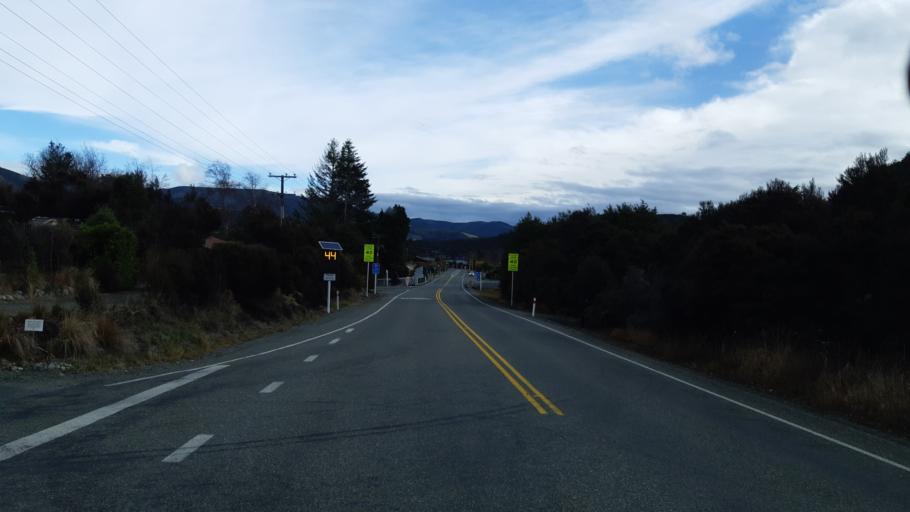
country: NZ
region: Tasman
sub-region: Tasman District
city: Wakefield
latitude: -41.8010
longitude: 172.8542
